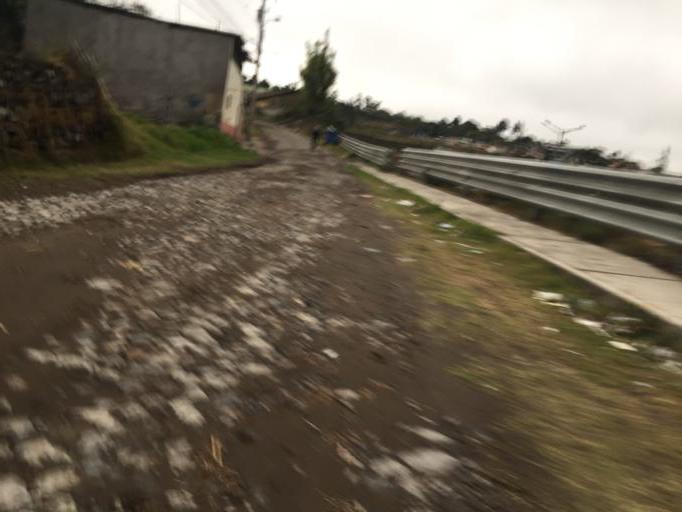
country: EC
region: Imbabura
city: Atuntaqui
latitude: 0.3386
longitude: -78.1718
